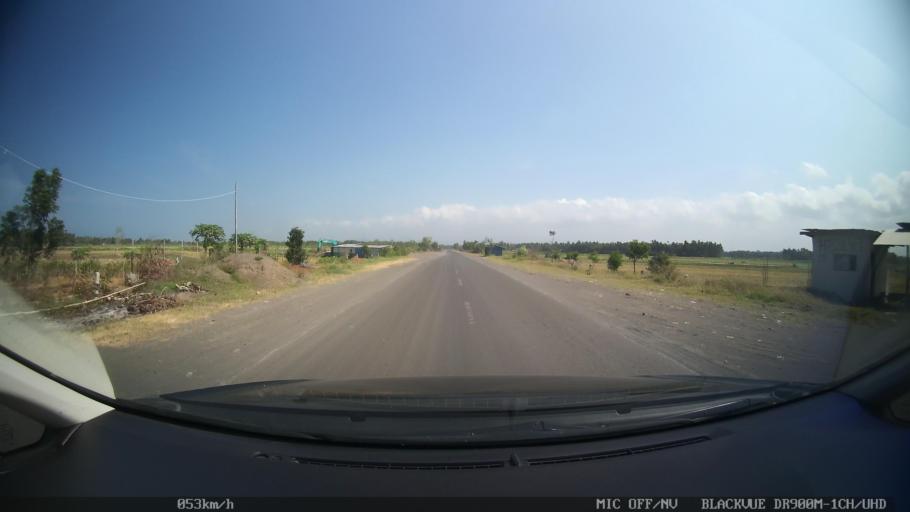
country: ID
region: Daerah Istimewa Yogyakarta
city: Srandakan
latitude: -7.9696
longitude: 110.2084
